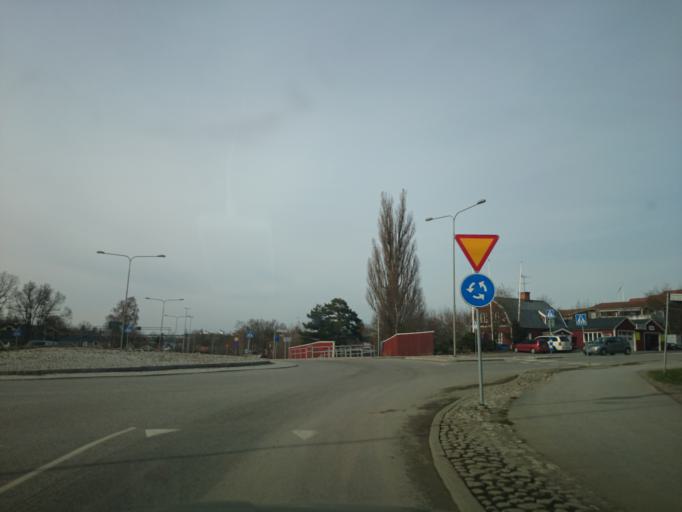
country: SE
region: Stockholm
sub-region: Huddinge Kommun
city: Segeltorp
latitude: 59.2794
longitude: 17.9432
